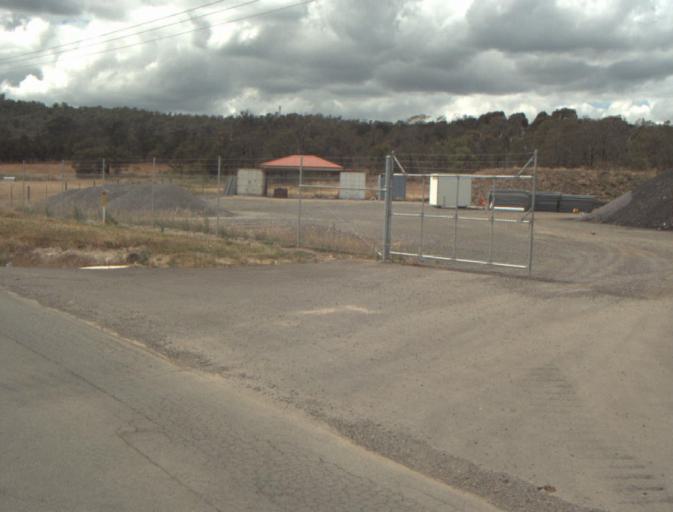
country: AU
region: Tasmania
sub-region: Launceston
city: Newnham
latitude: -41.4011
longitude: 147.1480
